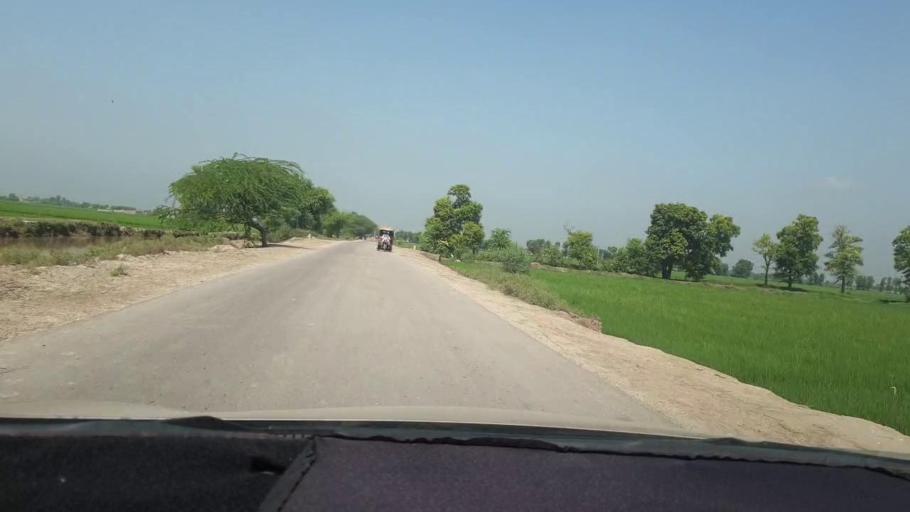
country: PK
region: Sindh
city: Miro Khan
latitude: 27.7686
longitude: 68.0677
